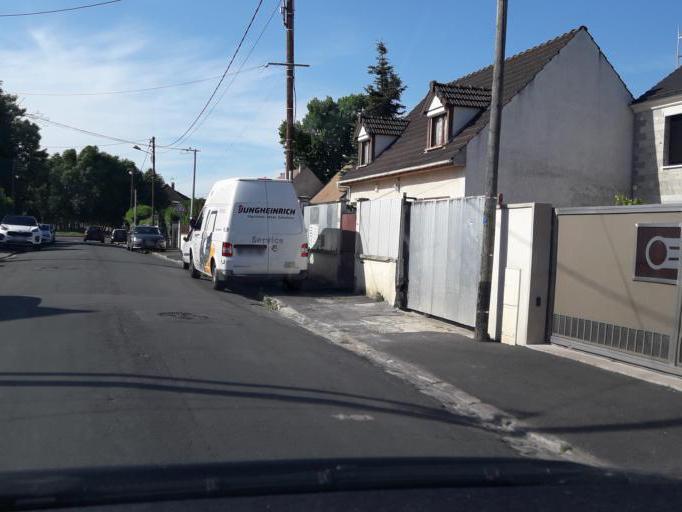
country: FR
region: Ile-de-France
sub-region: Departement de l'Essonne
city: Sainte-Genevieve-des-Bois
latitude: 48.6419
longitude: 2.3308
